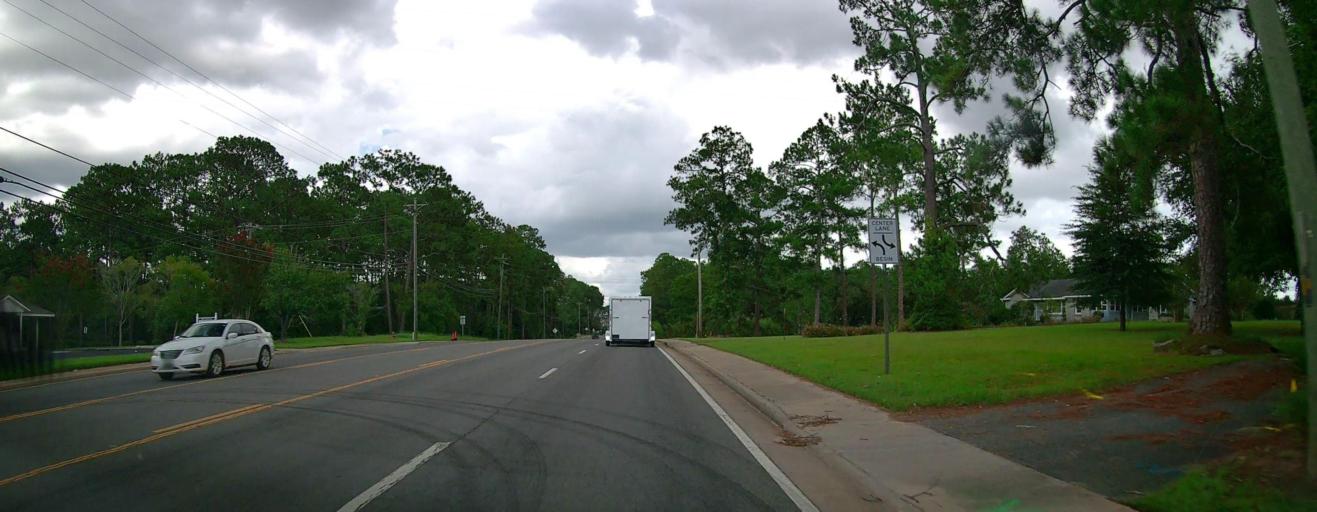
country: US
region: Georgia
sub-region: Coffee County
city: Douglas
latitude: 31.5160
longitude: -82.8798
